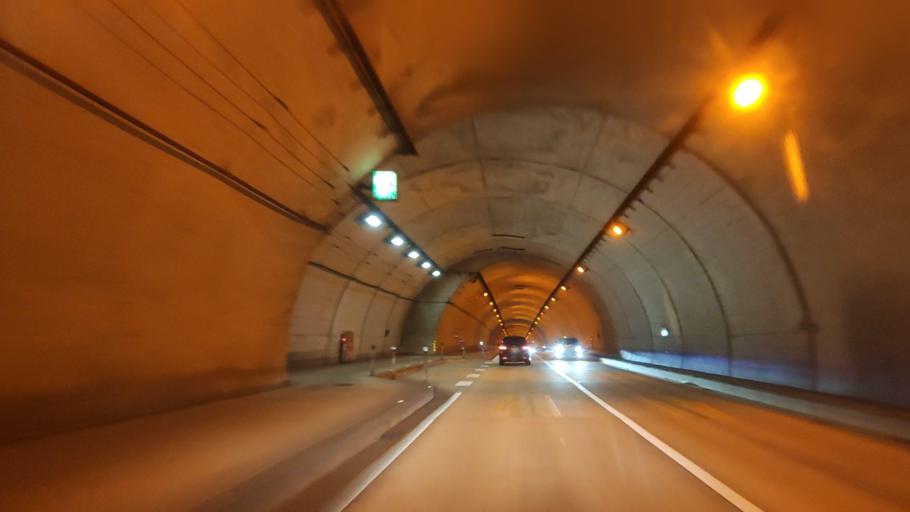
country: JP
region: Ehime
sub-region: Shikoku-chuo Shi
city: Matsuyama
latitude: 33.8817
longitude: 132.7106
